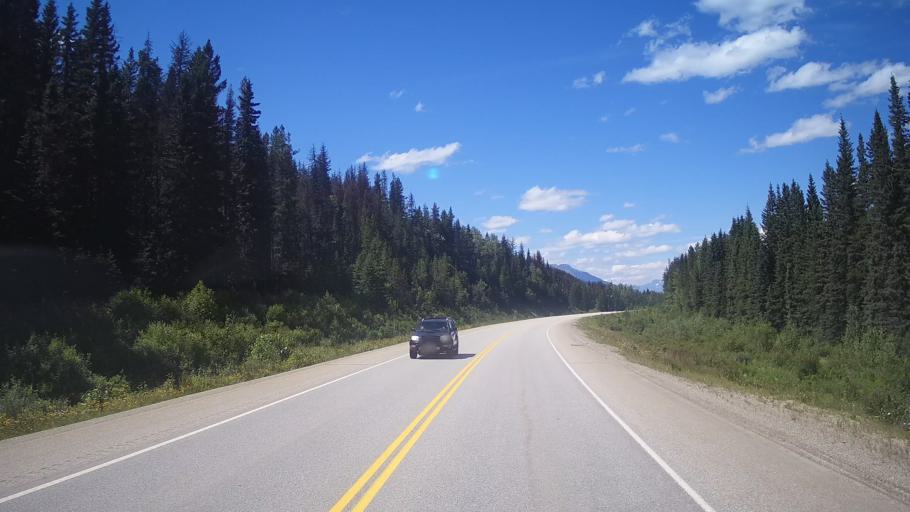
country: CA
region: Alberta
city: Jasper Park Lodge
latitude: 52.8641
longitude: -118.6647
